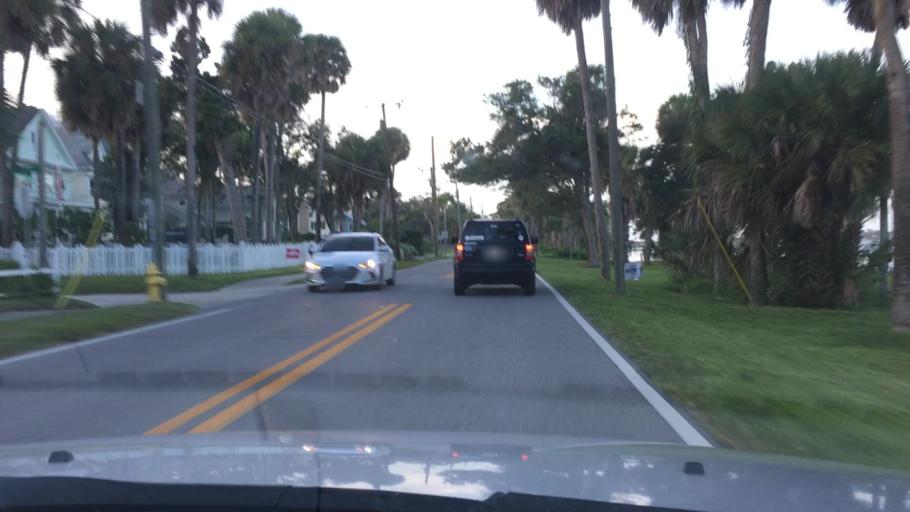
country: US
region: Florida
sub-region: Volusia County
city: Ormond Beach
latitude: 29.2887
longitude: -81.0568
